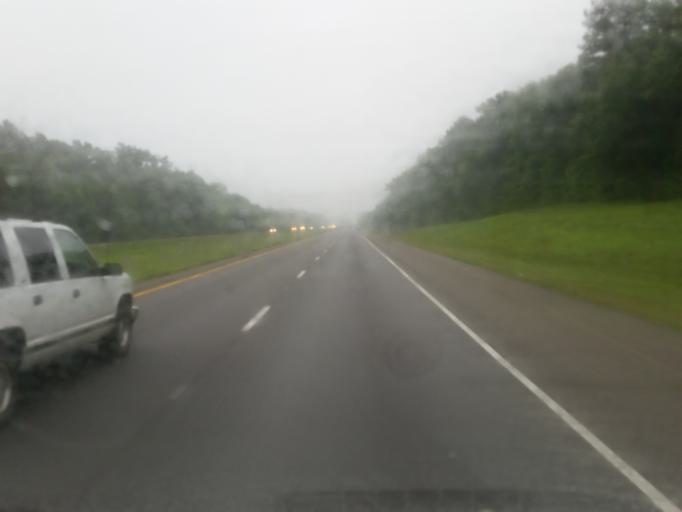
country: US
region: Louisiana
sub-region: Bossier Parish
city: Eastwood
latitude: 32.5418
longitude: -93.5901
